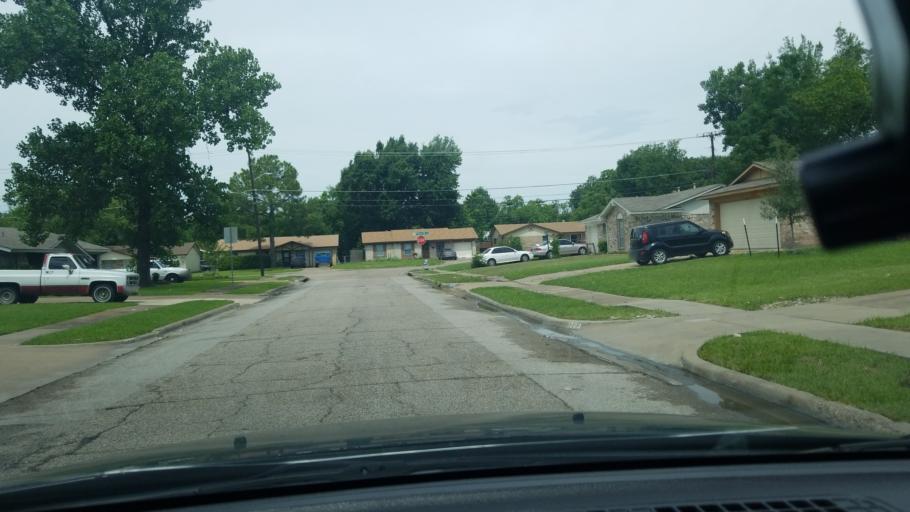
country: US
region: Texas
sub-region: Dallas County
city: Mesquite
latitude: 32.7558
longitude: -96.5828
